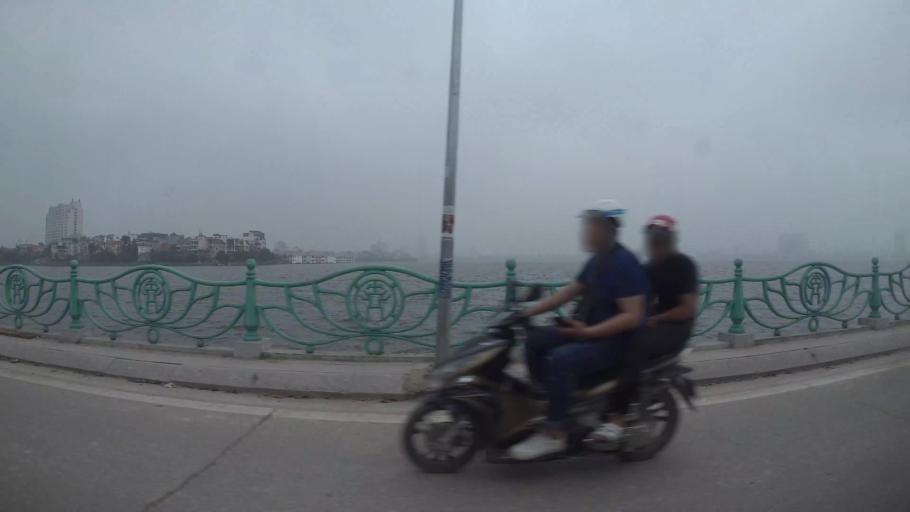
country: VN
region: Ha Noi
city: Tay Ho
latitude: 21.0591
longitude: 105.8260
